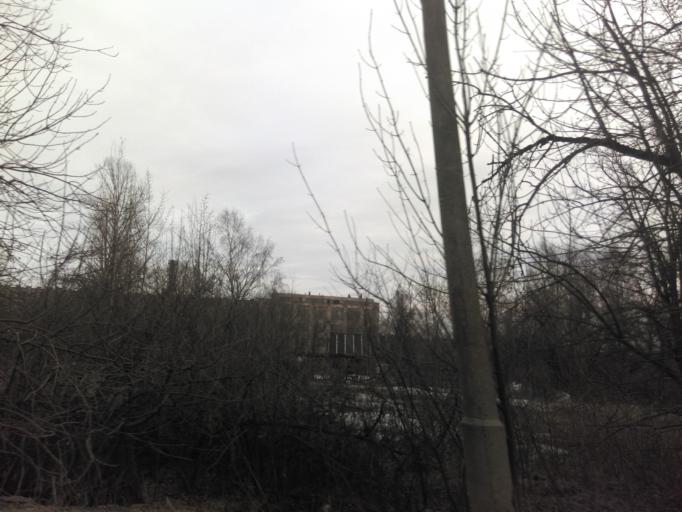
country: RU
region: Moskovskaya
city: Kolyubakino
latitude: 55.6717
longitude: 36.5395
